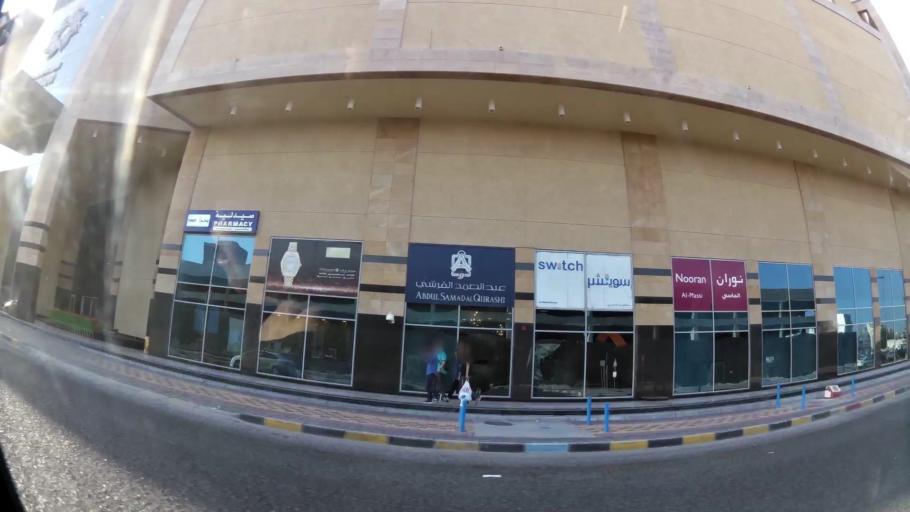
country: KW
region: Muhafazat Hawalli
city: As Salimiyah
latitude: 29.3355
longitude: 48.0631
